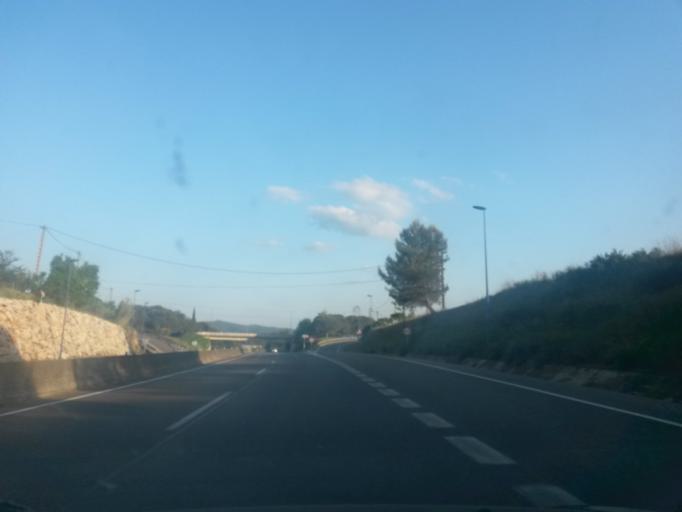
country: ES
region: Catalonia
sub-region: Provincia de Girona
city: Palol de Revardit
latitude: 42.0597
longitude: 2.8132
